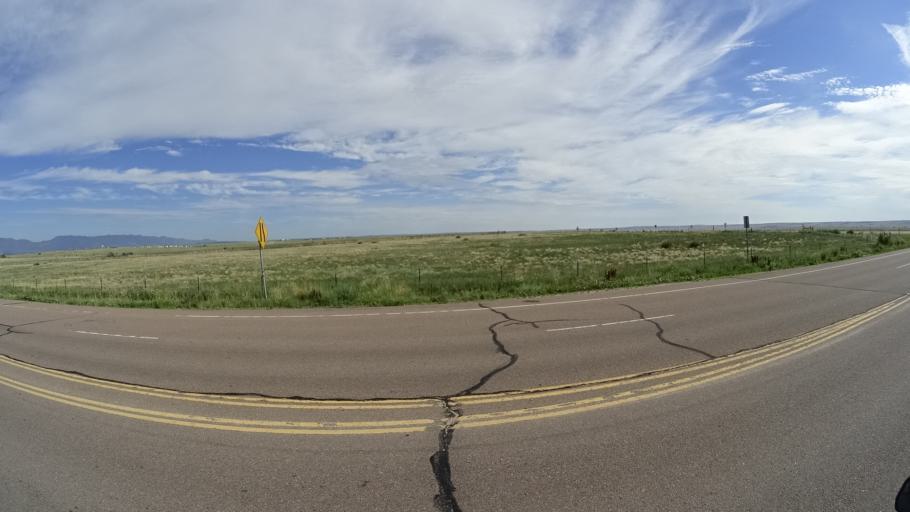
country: US
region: Colorado
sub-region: El Paso County
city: Security-Widefield
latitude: 38.7374
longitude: -104.6839
